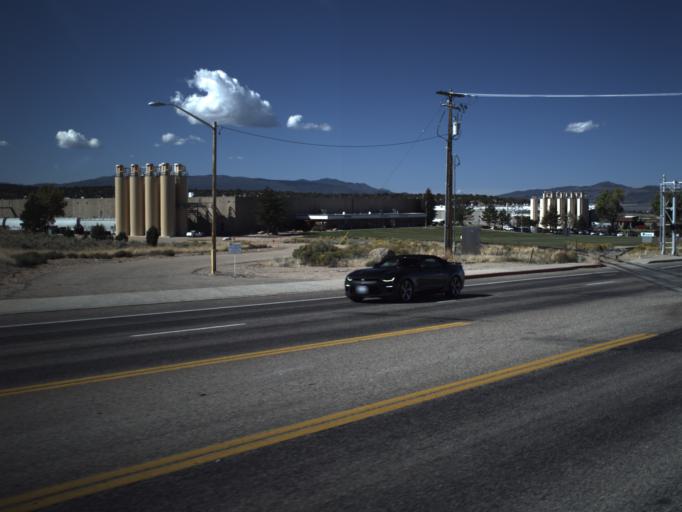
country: US
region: Utah
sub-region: Iron County
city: Cedar City
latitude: 37.6849
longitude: -113.0978
